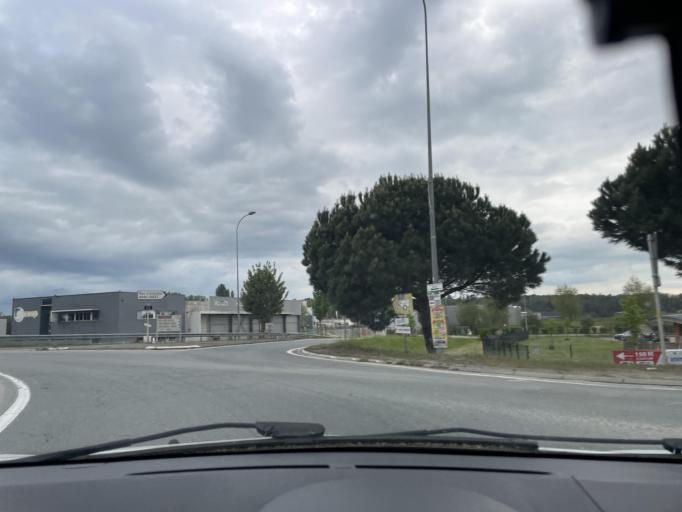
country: FR
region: Aquitaine
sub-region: Departement du Lot-et-Garonne
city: Fourques-sur-Garonne
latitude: 44.4365
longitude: 0.1309
